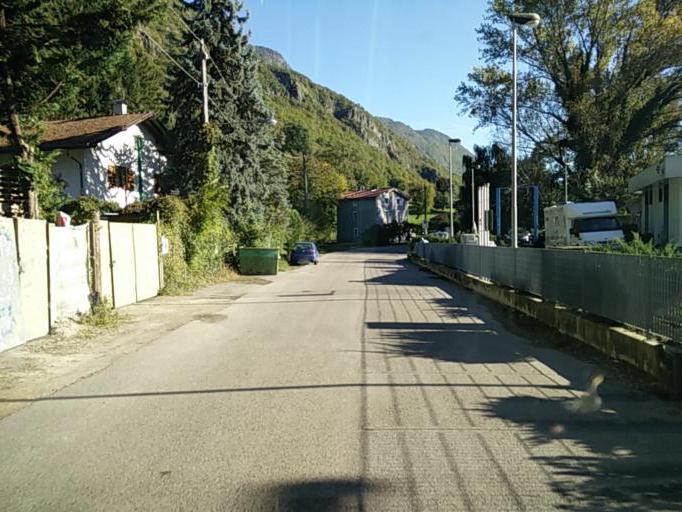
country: IT
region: Trentino-Alto Adige
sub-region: Bolzano
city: Sinigo
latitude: 46.6236
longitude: 11.1862
